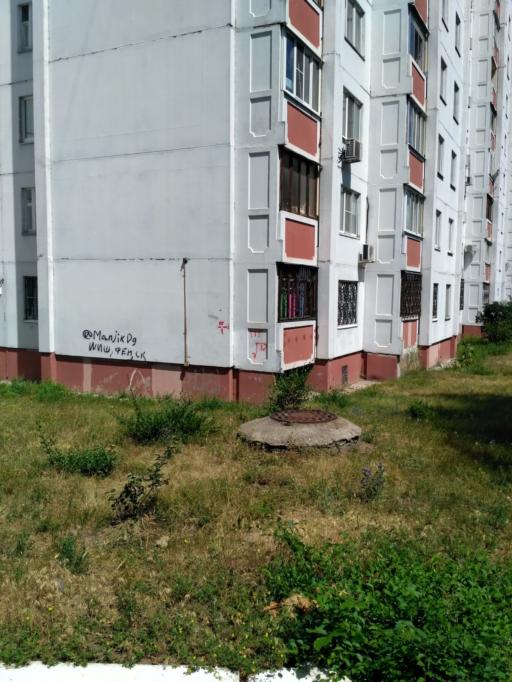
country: RU
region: Voronezj
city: Pridonskoy
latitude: 51.6576
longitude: 39.1255
